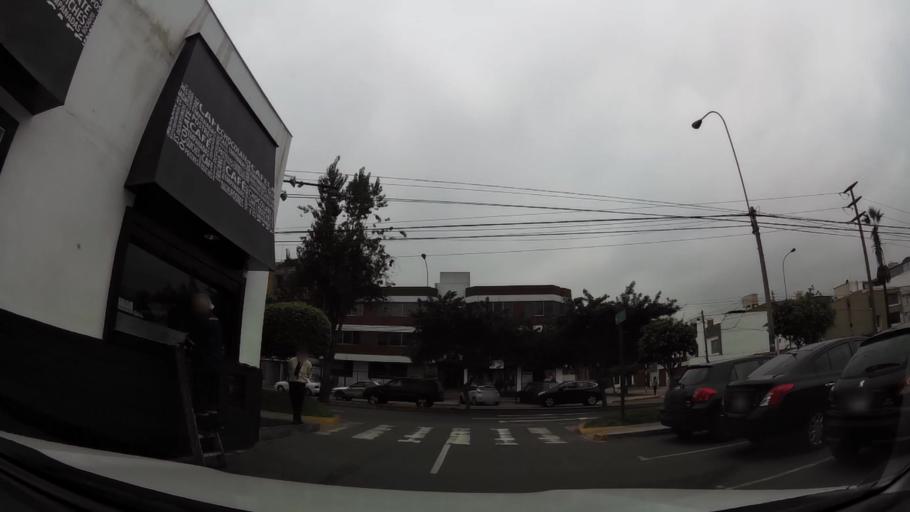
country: PE
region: Lima
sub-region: Lima
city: Surco
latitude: -12.1216
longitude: -76.9874
